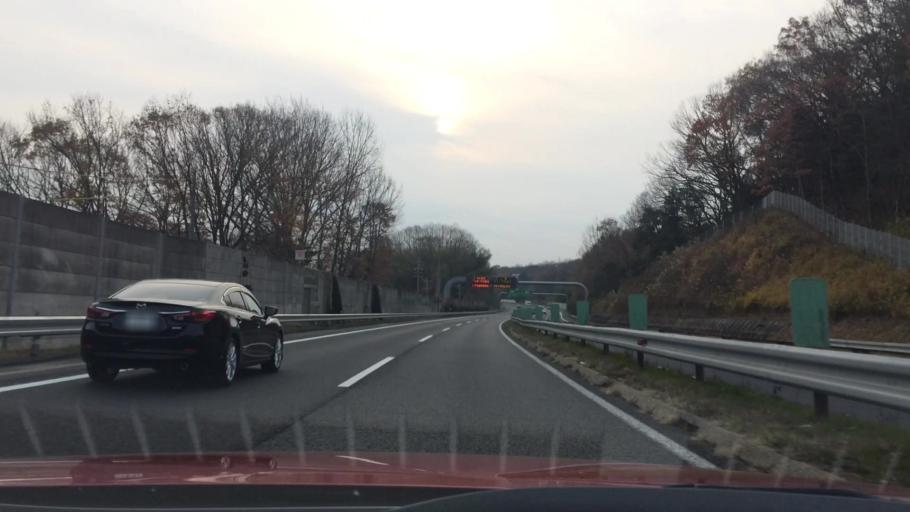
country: JP
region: Gifu
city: Toki
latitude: 35.3700
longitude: 137.1814
